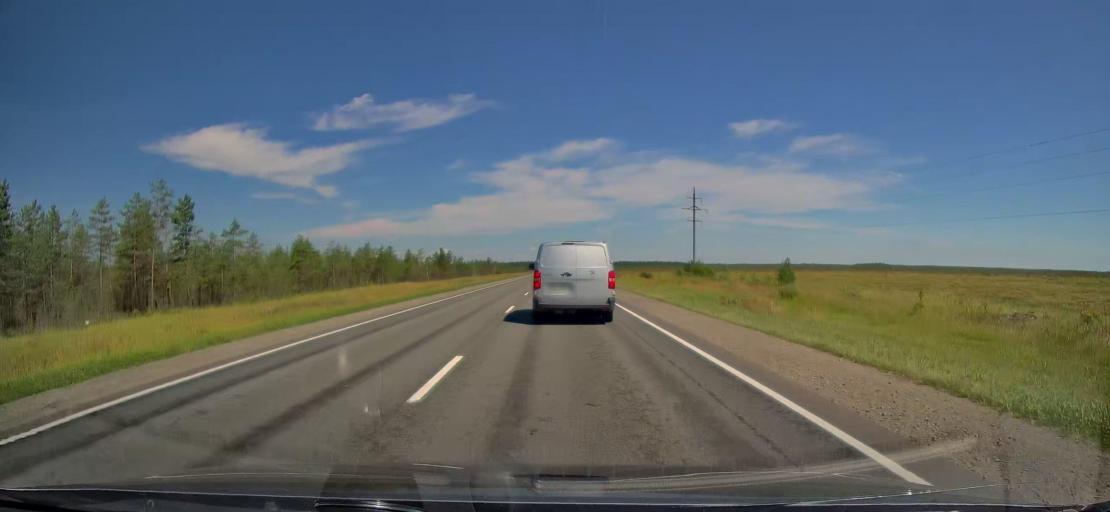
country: RU
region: Vologda
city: Khokhlovo
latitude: 58.9872
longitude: 37.3355
